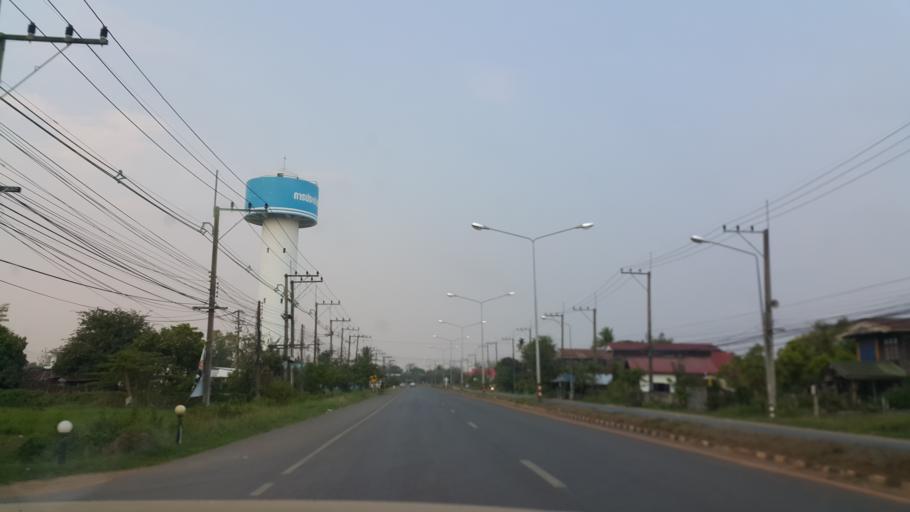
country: TH
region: Nakhon Phanom
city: That Phanom
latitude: 16.9795
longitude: 104.7277
